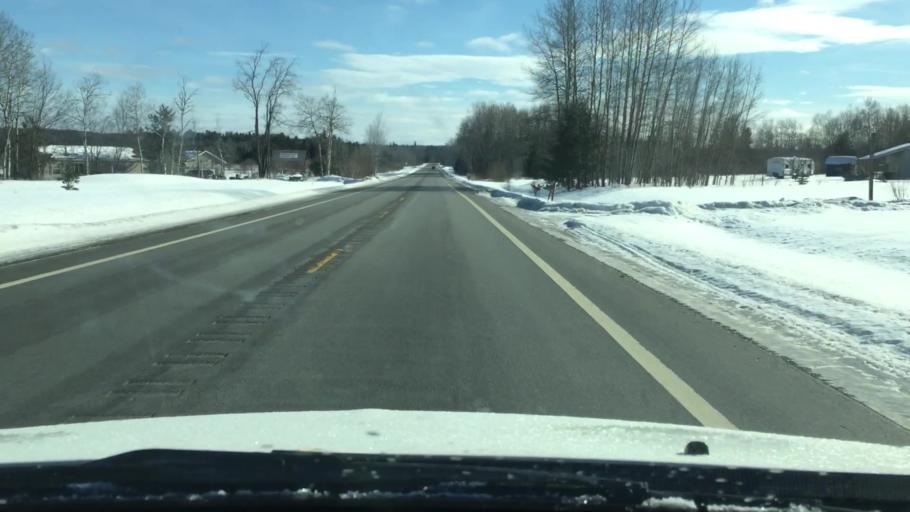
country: US
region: Michigan
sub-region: Charlevoix County
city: East Jordan
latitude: 45.0647
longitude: -85.0819
